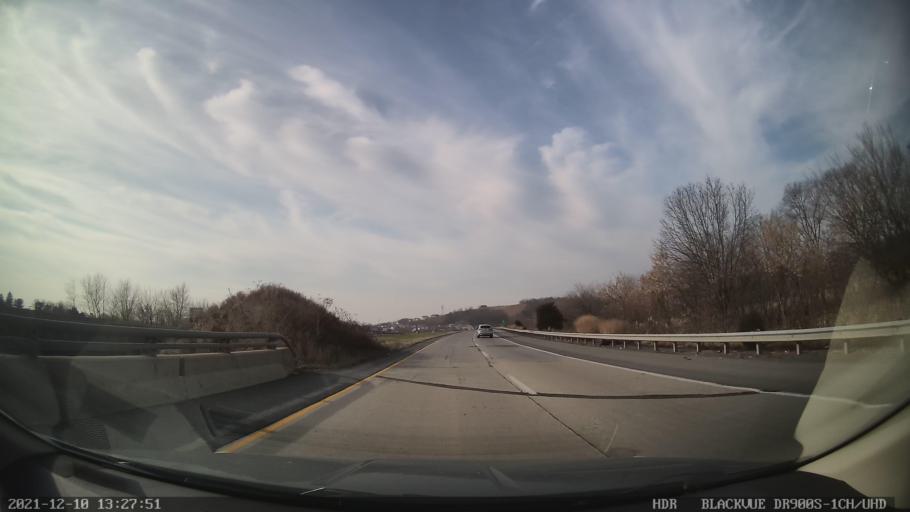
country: US
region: Pennsylvania
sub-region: Berks County
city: Kutztown
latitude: 40.5316
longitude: -75.7605
